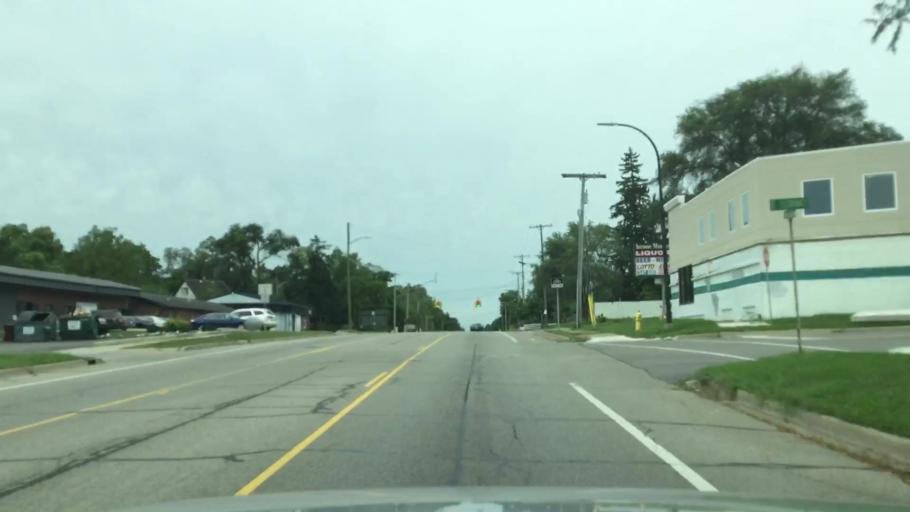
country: US
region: Michigan
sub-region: Washtenaw County
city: Ypsilanti
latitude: 42.2382
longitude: -83.6243
